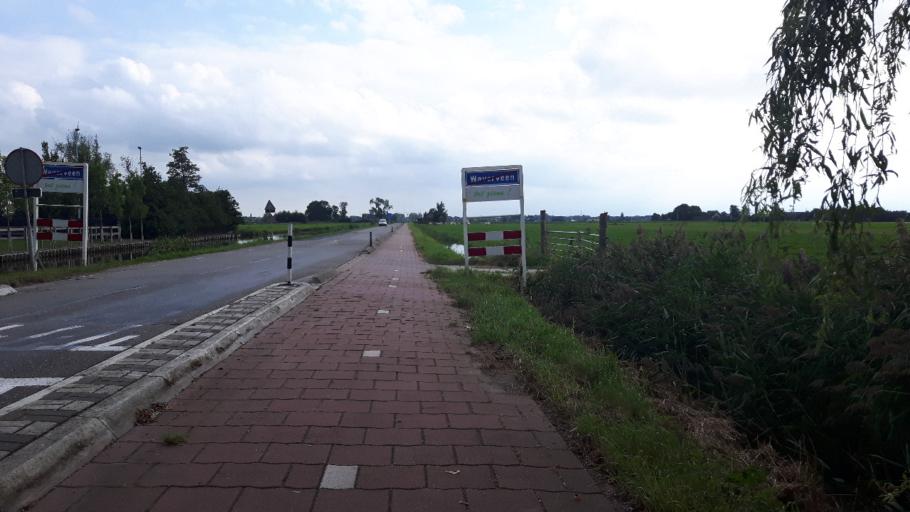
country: NL
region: Utrecht
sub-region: Gemeente De Ronde Venen
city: Mijdrecht
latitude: 52.2218
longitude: 4.9041
